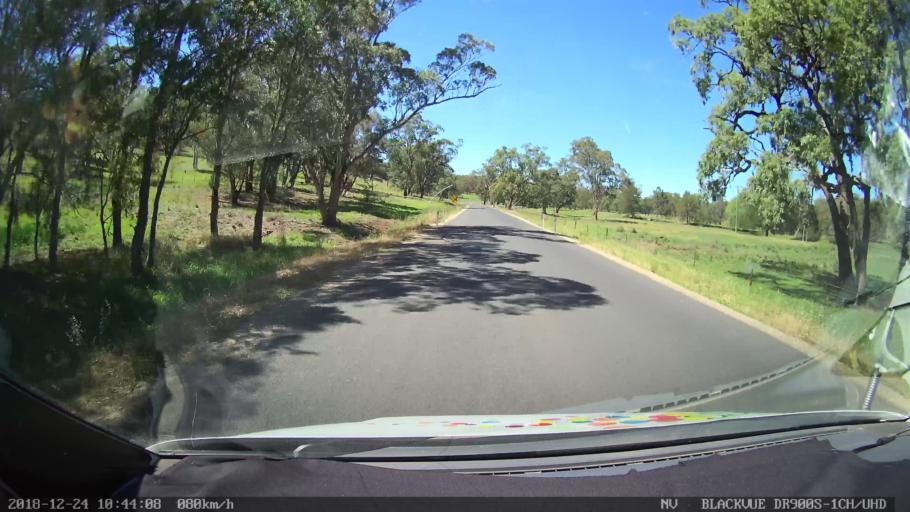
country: AU
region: New South Wales
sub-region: Upper Hunter Shire
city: Merriwa
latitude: -31.8897
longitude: 150.4439
